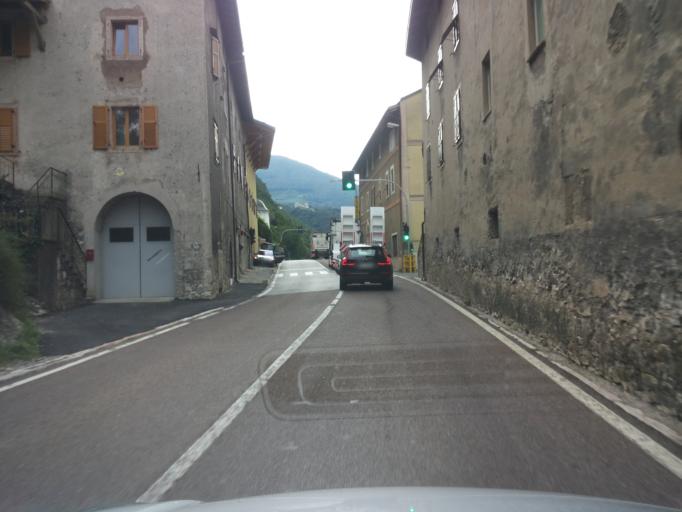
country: IT
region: Trentino-Alto Adige
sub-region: Provincia di Trento
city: Faedo
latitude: 46.2185
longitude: 11.1534
